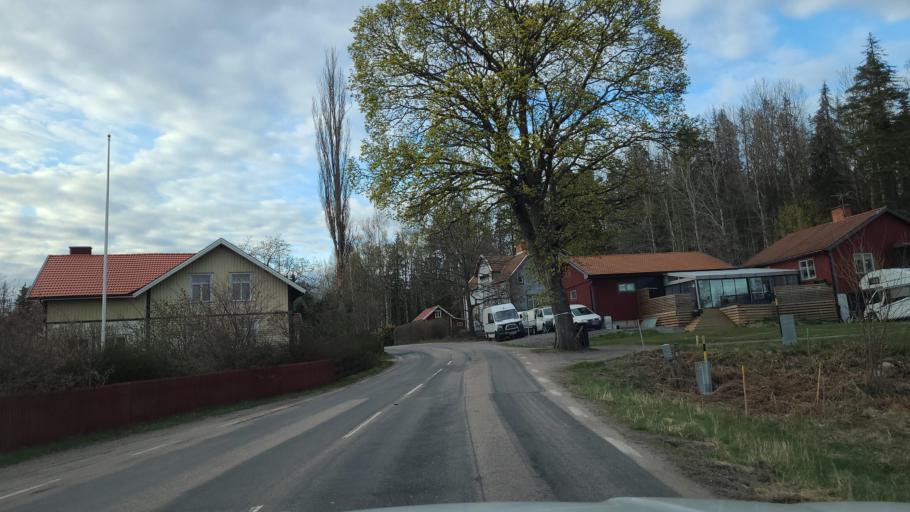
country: SE
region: Soedermanland
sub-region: Nykopings Kommun
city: Olstorp
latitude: 58.6927
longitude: 16.6368
